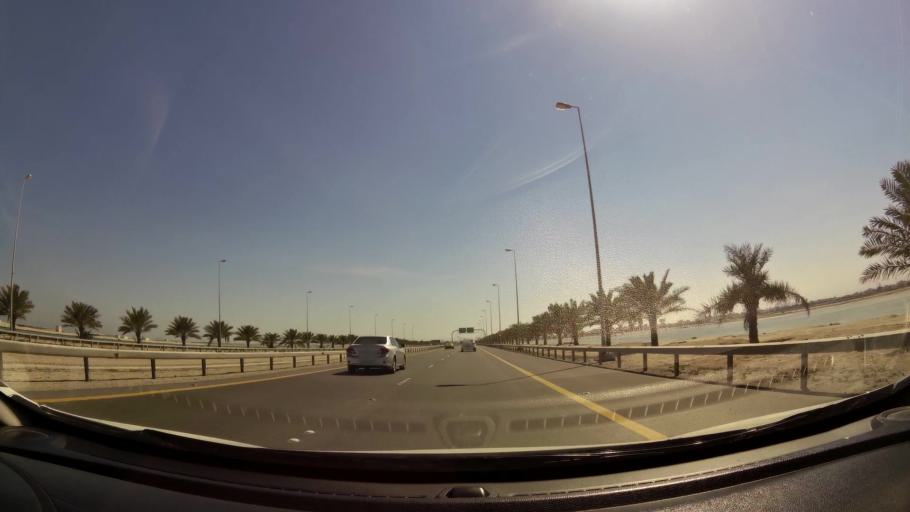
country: BH
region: Muharraq
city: Al Hadd
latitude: 26.2611
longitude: 50.6607
